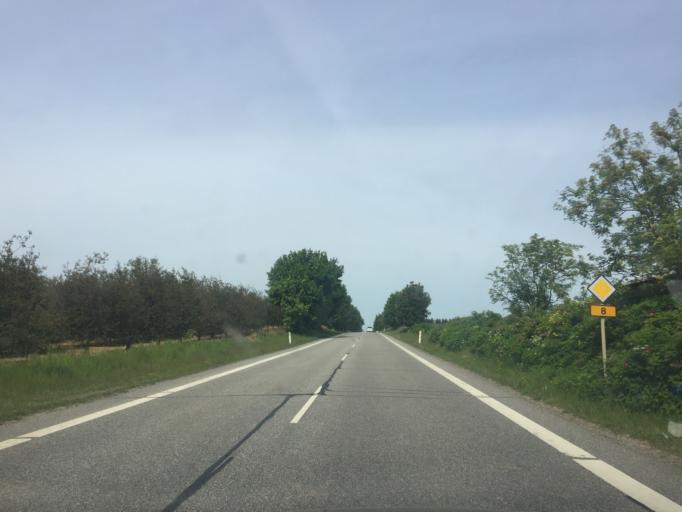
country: DK
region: South Denmark
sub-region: Nyborg Kommune
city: Nyborg
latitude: 55.3084
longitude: 10.7274
